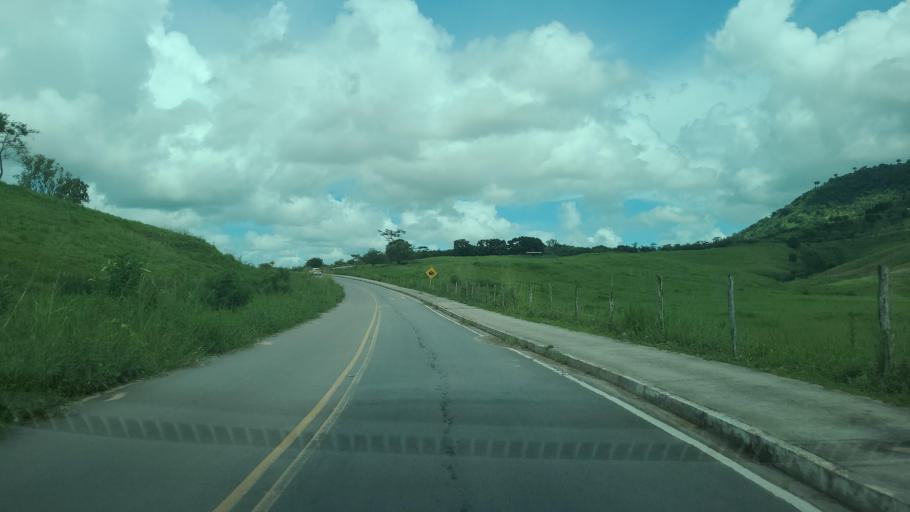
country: BR
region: Alagoas
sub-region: Uniao Dos Palmares
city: Uniao dos Palmares
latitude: -9.1660
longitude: -36.0569
